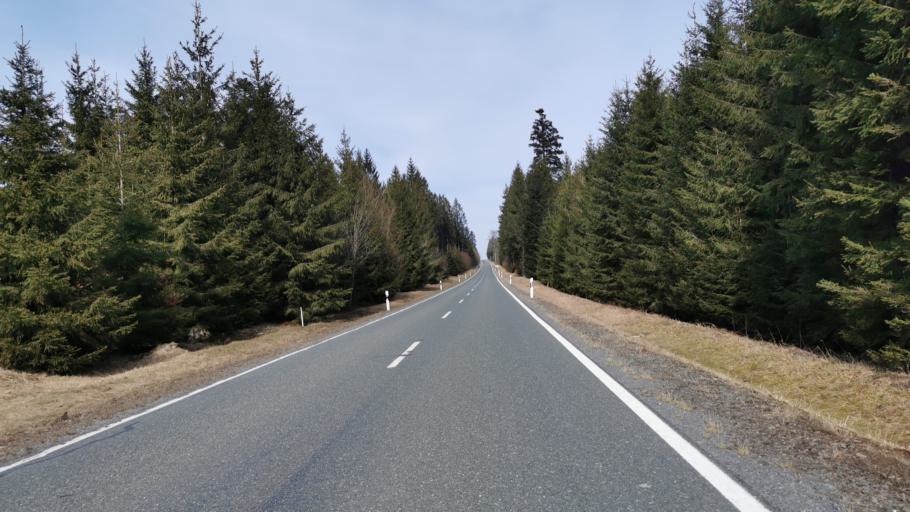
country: DE
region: Bavaria
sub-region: Upper Franconia
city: Tschirn
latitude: 50.4221
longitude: 11.4560
